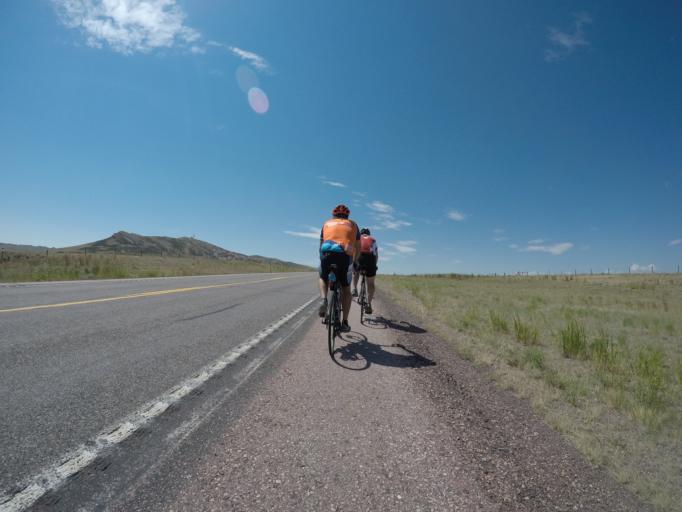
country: US
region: Wyoming
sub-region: Albany County
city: Laramie
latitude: 41.6598
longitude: -105.5341
